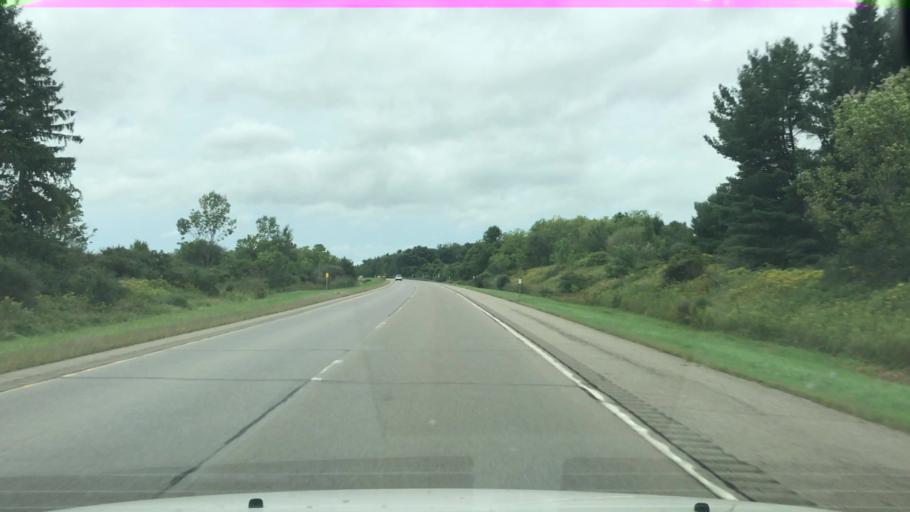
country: US
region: New York
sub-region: Erie County
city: North Boston
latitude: 42.6148
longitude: -78.7618
